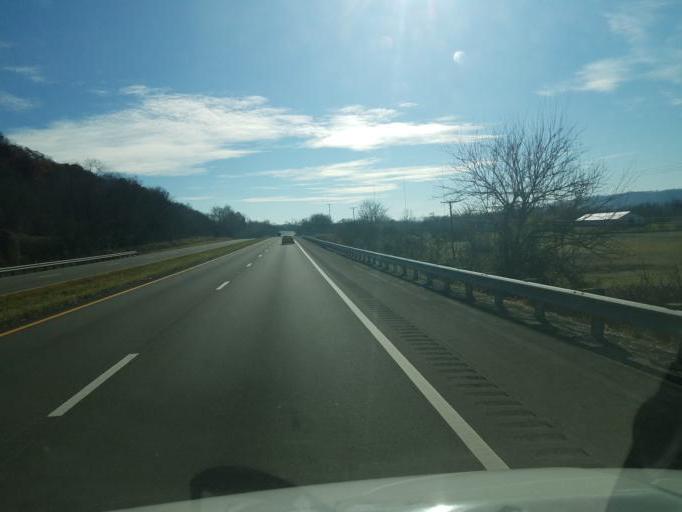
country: US
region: Ohio
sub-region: Scioto County
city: Rosemount
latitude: 38.8159
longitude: -82.9848
